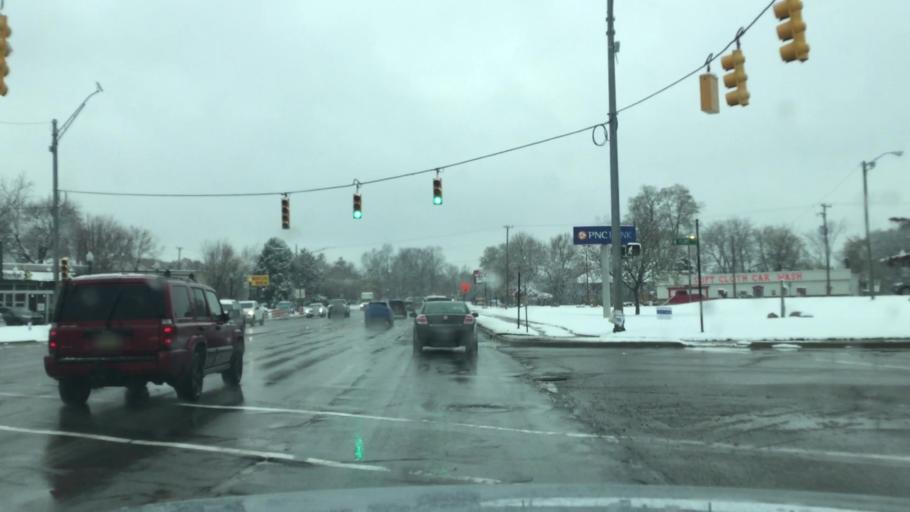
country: US
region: Michigan
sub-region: Oakland County
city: Lake Orion
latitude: 42.7845
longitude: -83.2419
